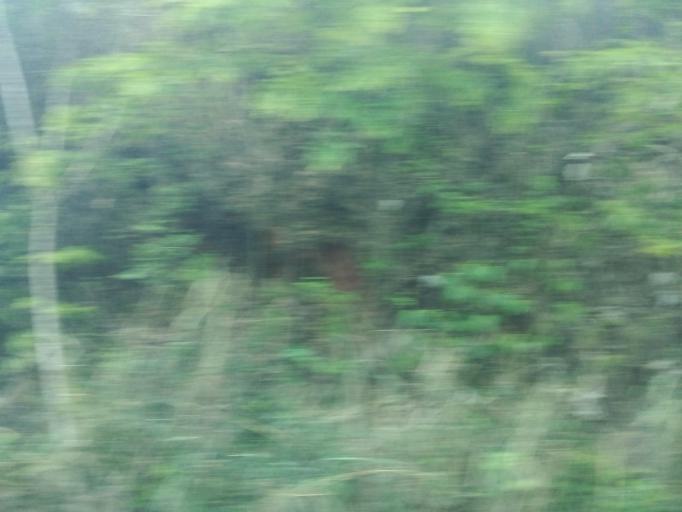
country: BR
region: Minas Gerais
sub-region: Nova Era
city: Nova Era
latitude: -19.6747
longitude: -42.8958
